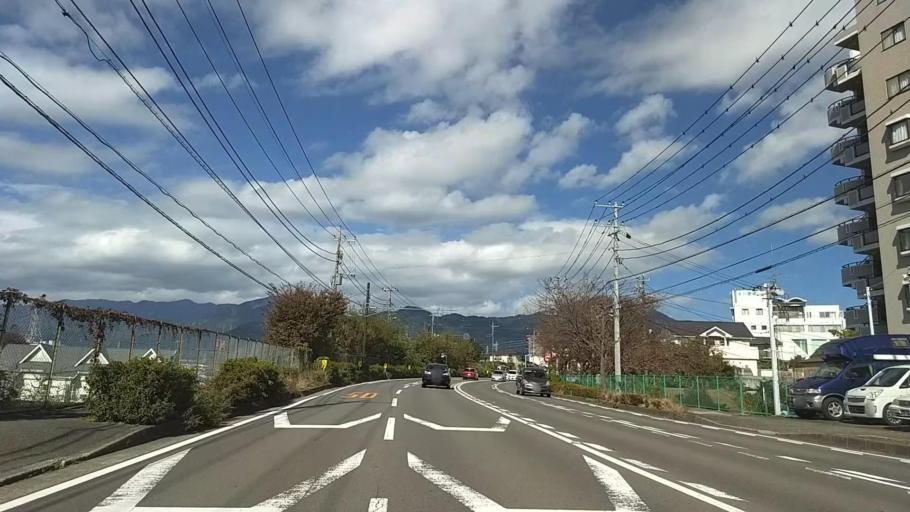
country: JP
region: Kanagawa
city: Hadano
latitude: 35.3727
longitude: 139.2353
